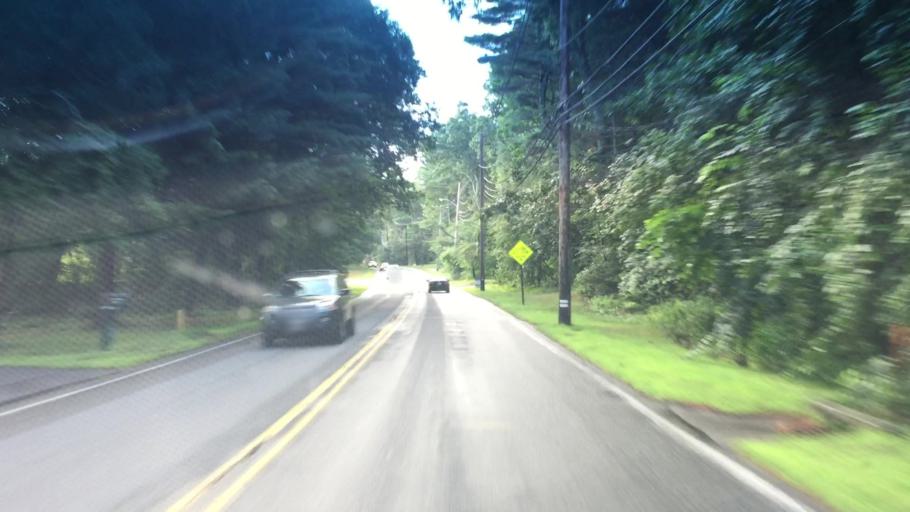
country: US
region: Massachusetts
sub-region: Norfolk County
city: Medfield
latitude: 42.1668
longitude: -71.2924
